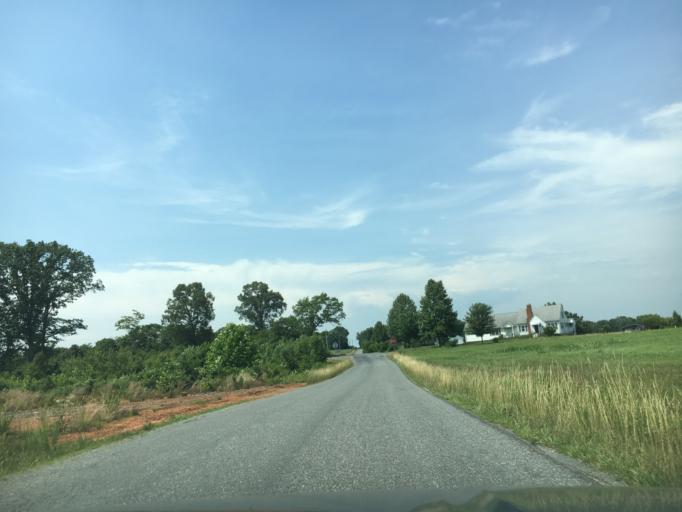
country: US
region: Virginia
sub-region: Pittsylvania County
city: Chatham
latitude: 36.8894
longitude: -79.4059
